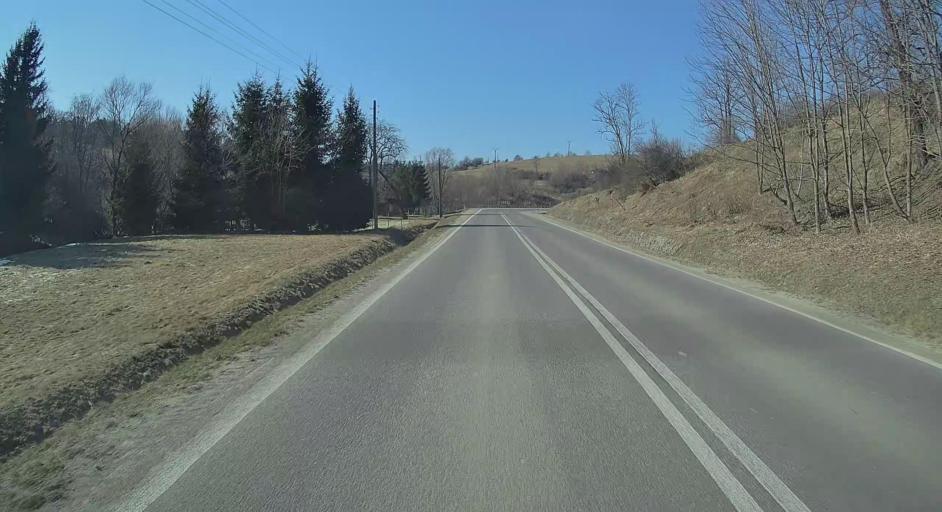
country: PL
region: Subcarpathian Voivodeship
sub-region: Powiat bieszczadzki
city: Ustrzyki Dolne
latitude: 49.4944
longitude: 22.6368
